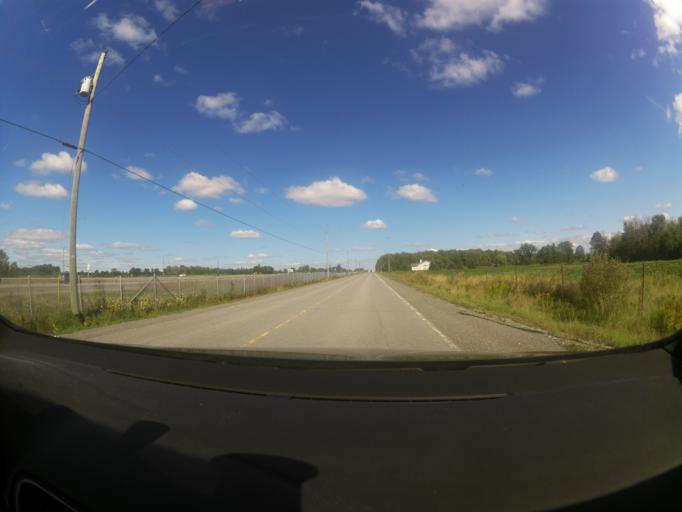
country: CA
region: Ontario
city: Carleton Place
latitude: 45.1563
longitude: -76.0800
